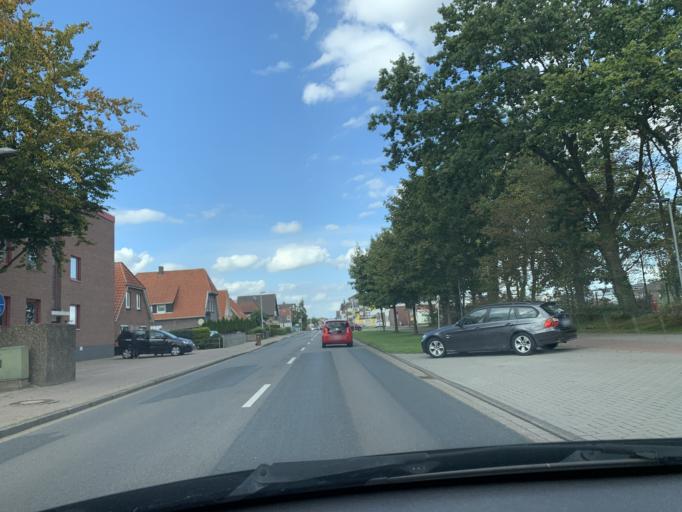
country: DE
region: Lower Saxony
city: Bad Zwischenahn
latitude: 53.1794
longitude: 7.9965
